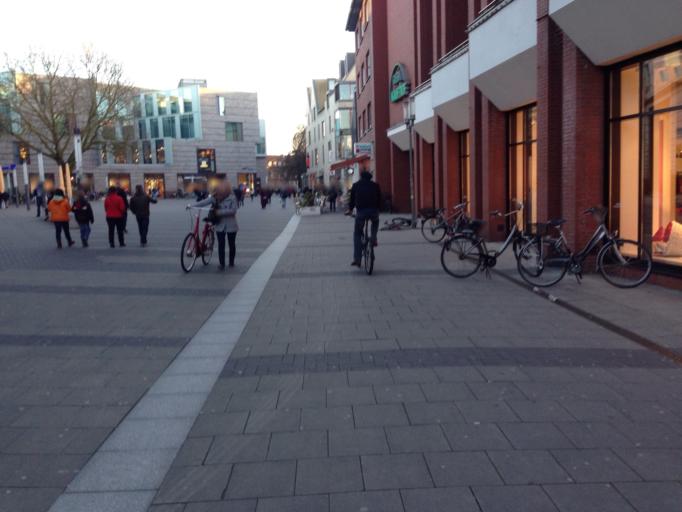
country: DE
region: North Rhine-Westphalia
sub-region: Regierungsbezirk Munster
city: Muenster
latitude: 51.9608
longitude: 7.6294
